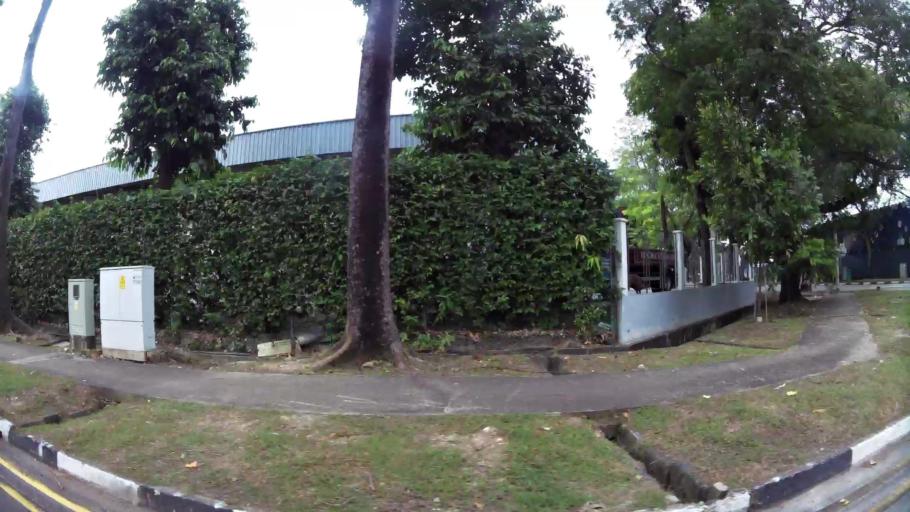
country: MY
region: Johor
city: Johor Bahru
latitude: 1.3092
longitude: 103.6651
